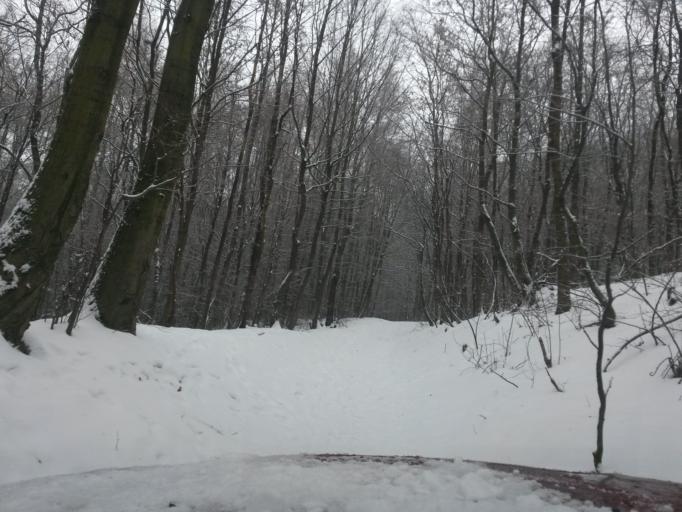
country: SK
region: Kosicky
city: Kosice
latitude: 48.7223
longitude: 21.3068
